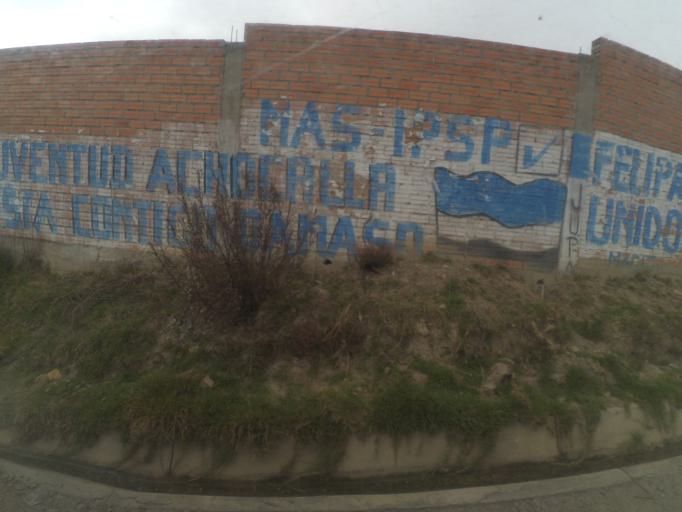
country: BO
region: La Paz
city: La Paz
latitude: -16.5716
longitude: -68.1741
